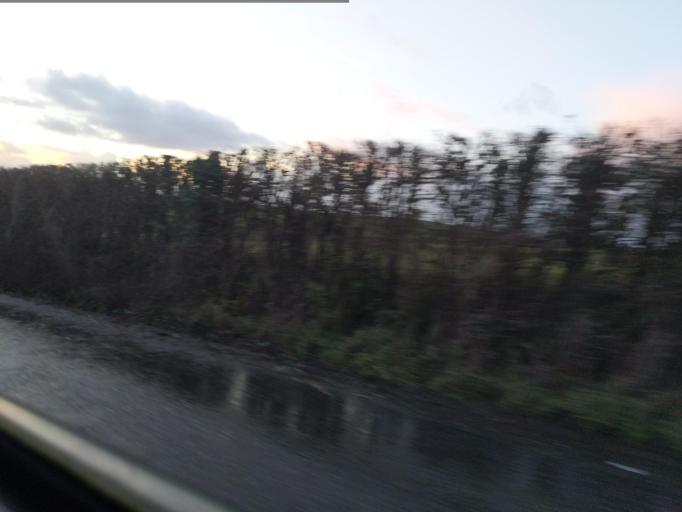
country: GB
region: England
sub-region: Devon
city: Fremington
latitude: 51.0518
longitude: -4.0890
